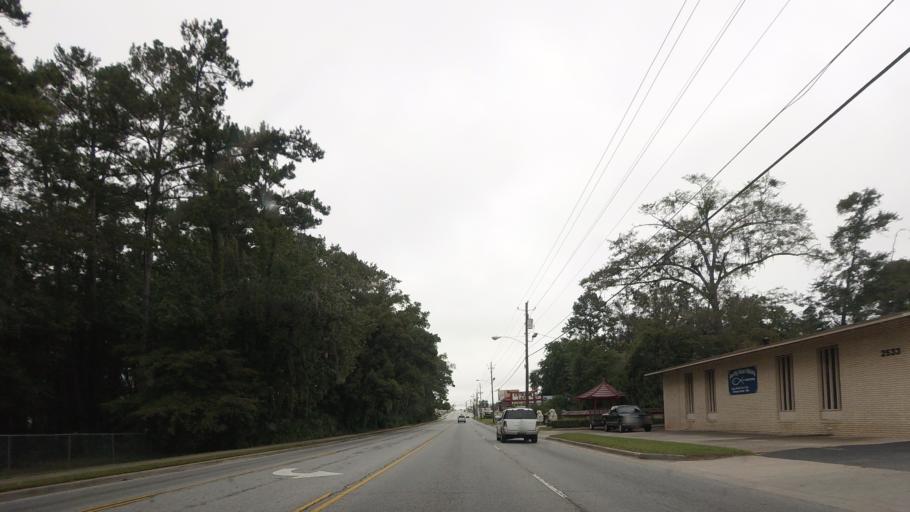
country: US
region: Georgia
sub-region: Lowndes County
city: Remerton
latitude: 30.8662
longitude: -83.2858
